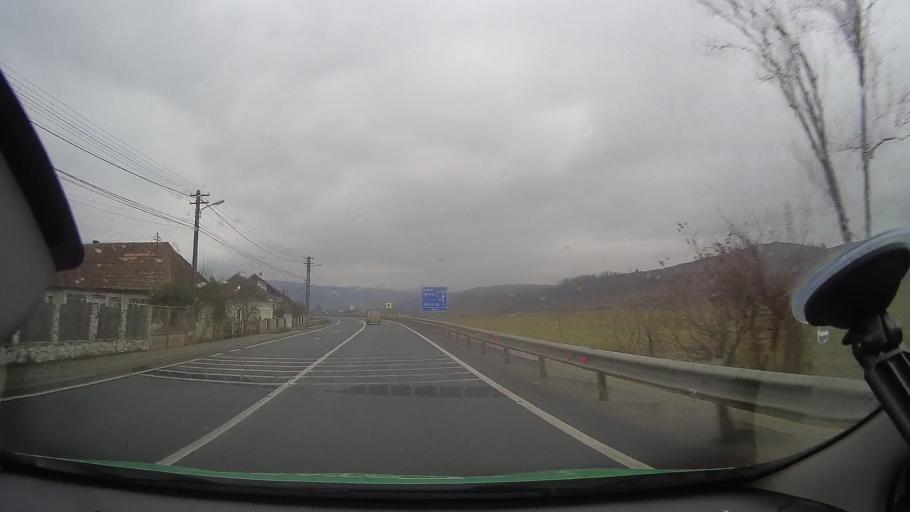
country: RO
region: Hunedoara
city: Vata de Jos
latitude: 46.1918
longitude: 22.6143
